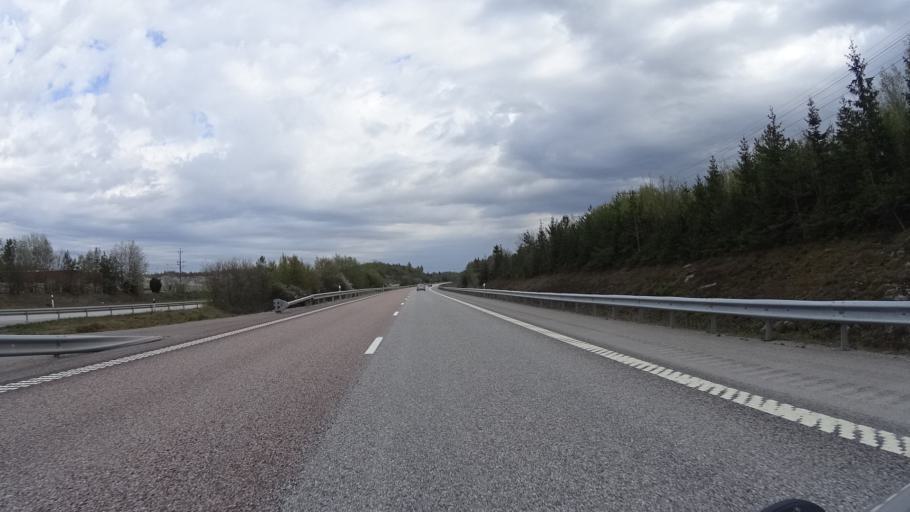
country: SE
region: Stockholm
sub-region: Nykvarns Kommun
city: Nykvarn
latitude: 59.2047
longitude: 17.3510
